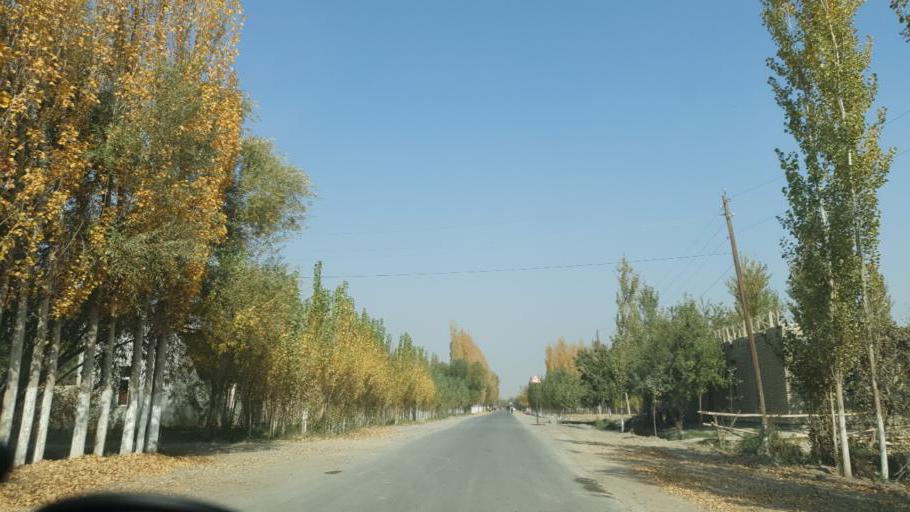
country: UZ
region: Fergana
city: Beshariq
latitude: 40.4898
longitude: 70.6205
